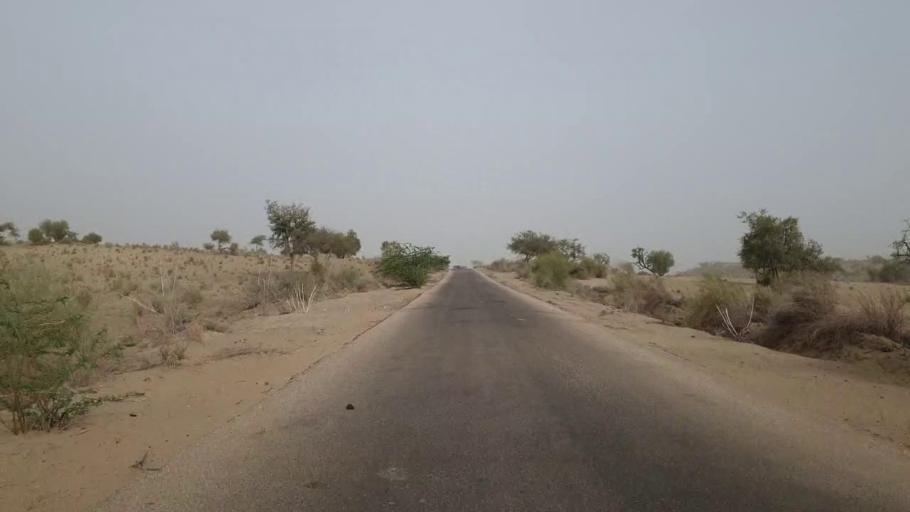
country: PK
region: Sindh
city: Islamkot
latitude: 24.5843
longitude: 70.2974
